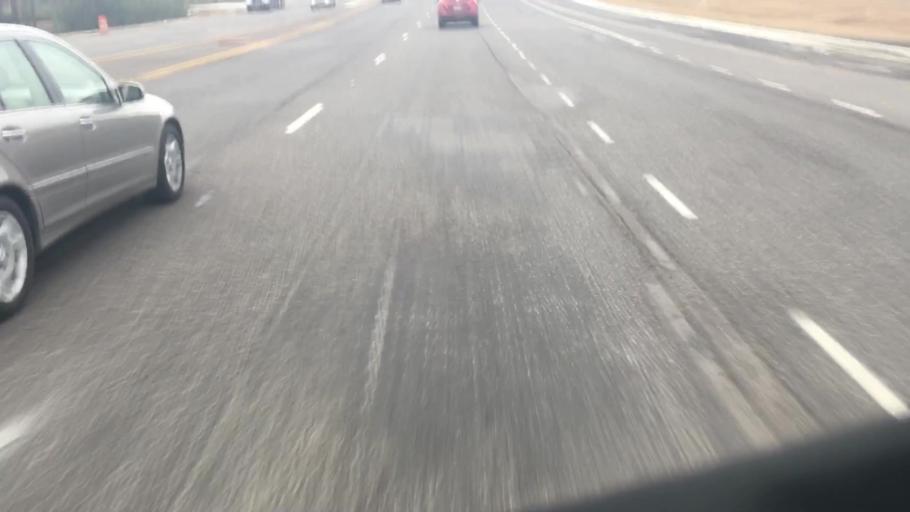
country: US
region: Alabama
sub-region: Shelby County
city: Helena
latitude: 33.3557
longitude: -86.8491
